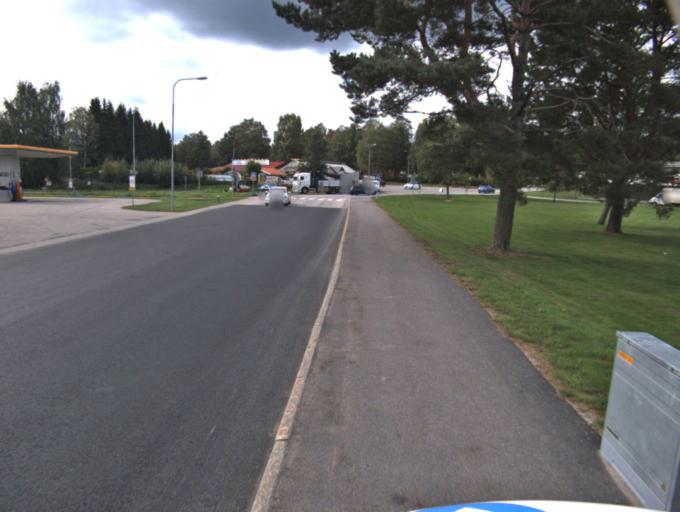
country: SE
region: Vaestra Goetaland
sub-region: Ulricehamns Kommun
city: Ulricehamn
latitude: 57.8041
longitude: 13.4080
